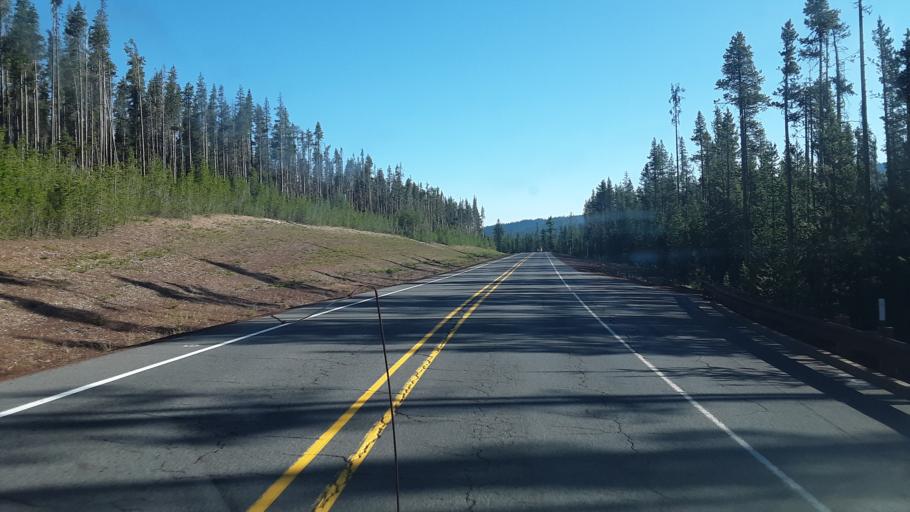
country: US
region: Oregon
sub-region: Lane County
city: Oakridge
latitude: 43.1023
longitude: -122.1304
